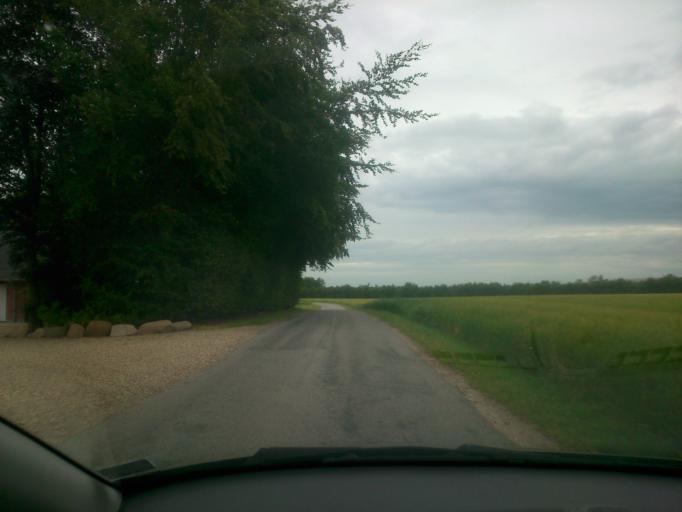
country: DK
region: South Denmark
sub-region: Esbjerg Kommune
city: Esbjerg
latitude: 55.5505
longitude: 8.4194
